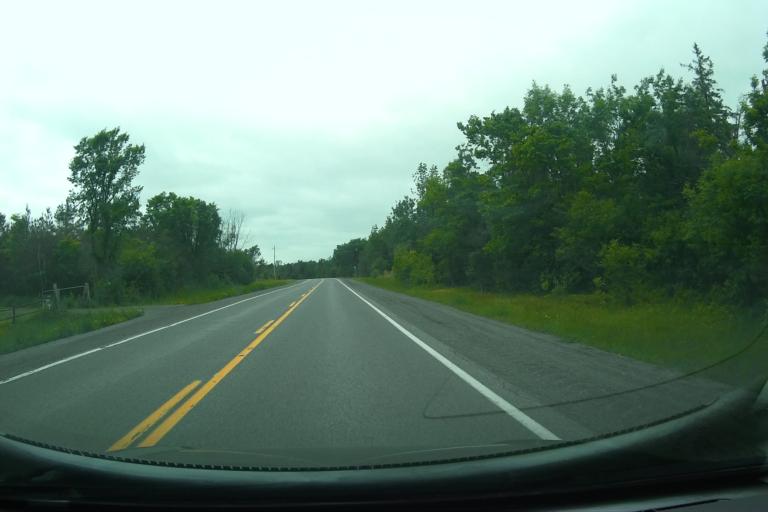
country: CA
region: Ontario
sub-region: Lanark County
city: Smiths Falls
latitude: 45.0155
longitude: -75.8410
